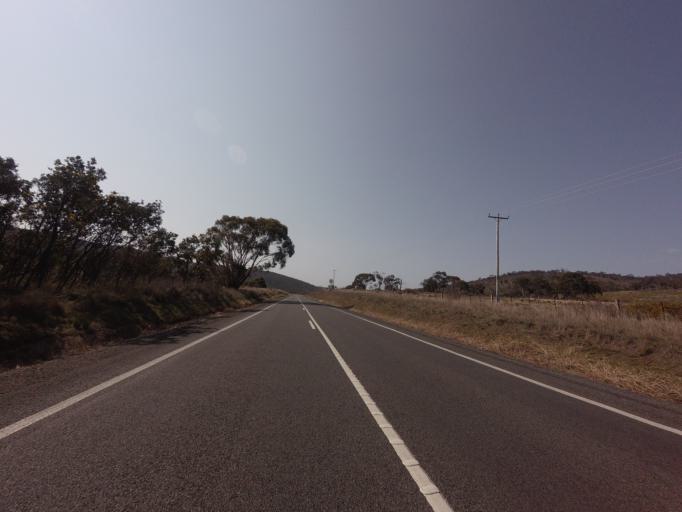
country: AU
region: Tasmania
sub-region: Northern Midlands
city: Evandale
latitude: -41.8142
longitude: 147.5812
